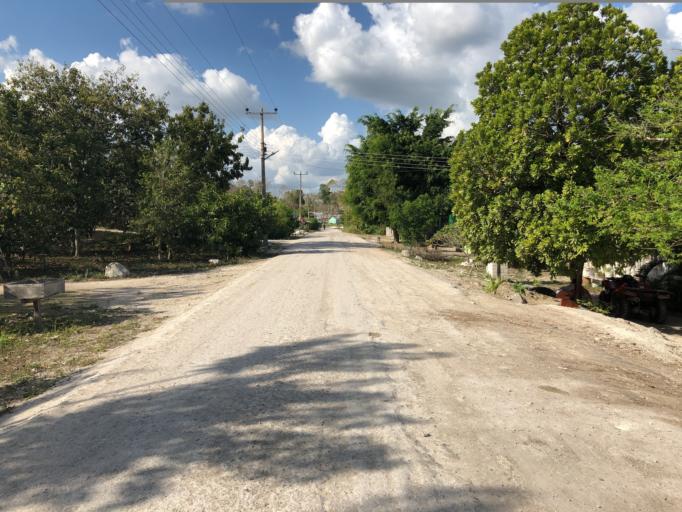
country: MX
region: Quintana Roo
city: Nicolas Bravo
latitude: 18.4489
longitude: -89.3072
